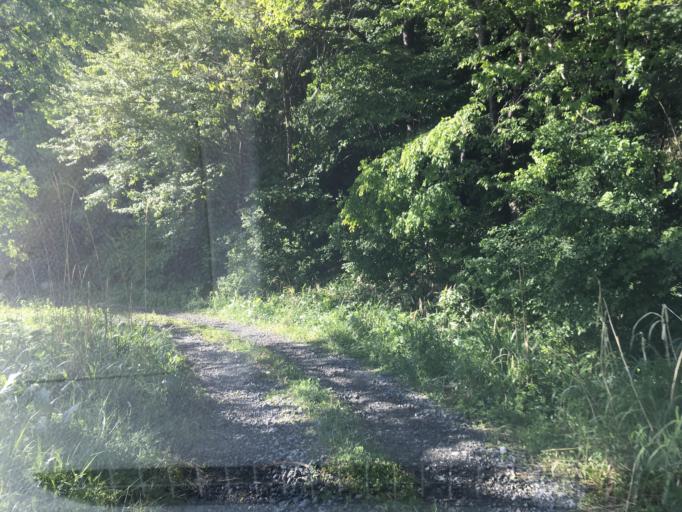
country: JP
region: Iwate
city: Ichinoseki
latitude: 38.8710
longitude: 141.4497
